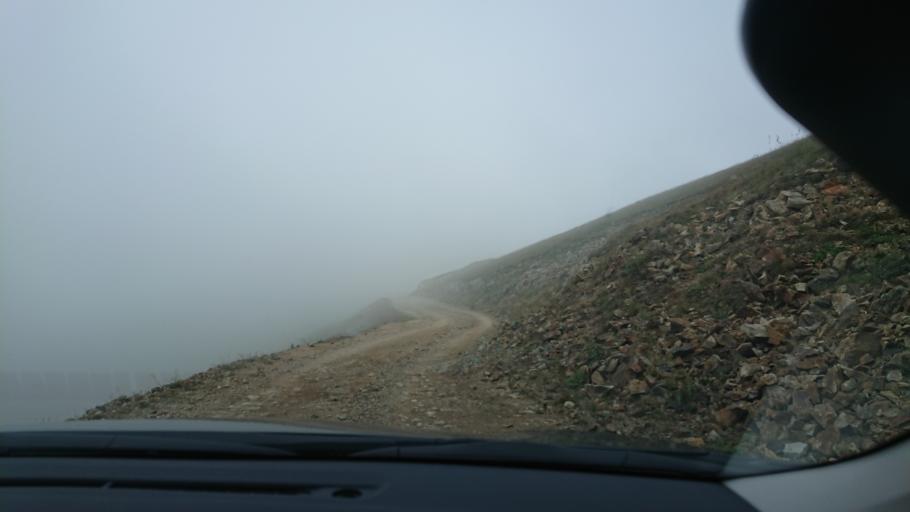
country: TR
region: Gumushane
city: Kurtun
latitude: 40.6264
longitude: 38.9942
